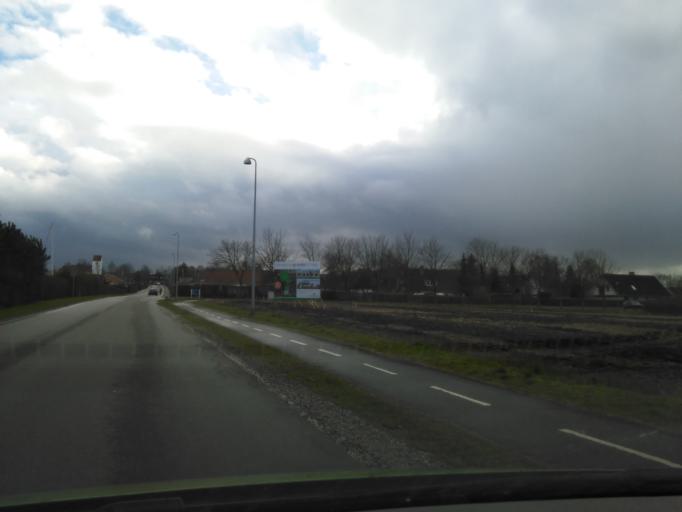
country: DK
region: Central Jutland
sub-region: Skanderborg Kommune
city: Skovby
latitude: 56.1206
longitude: 9.9539
